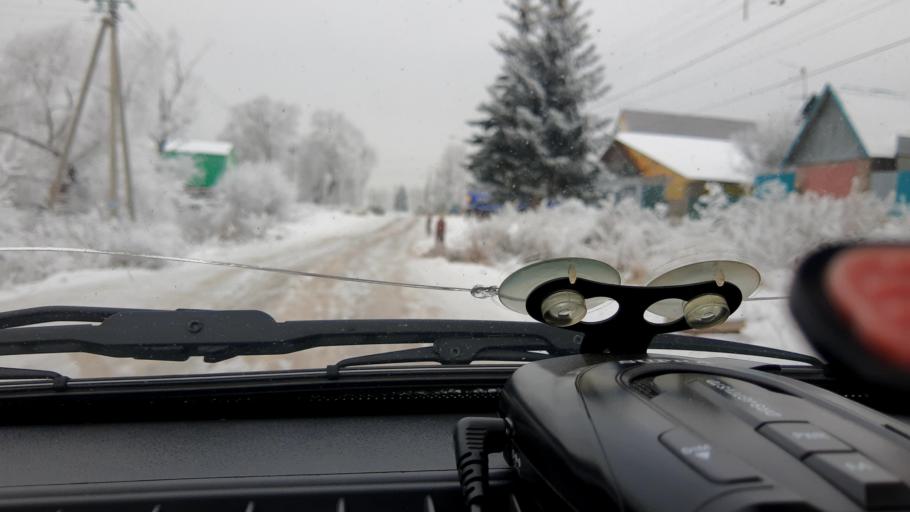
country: RU
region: Bashkortostan
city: Iglino
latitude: 54.7830
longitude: 56.2309
